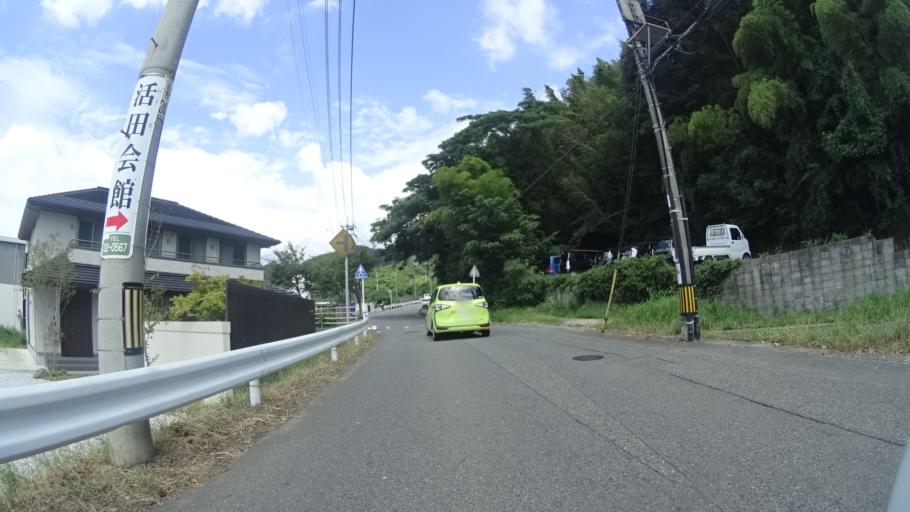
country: JP
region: Yamaguchi
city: Shimonoseki
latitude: 33.9794
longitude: 130.9510
